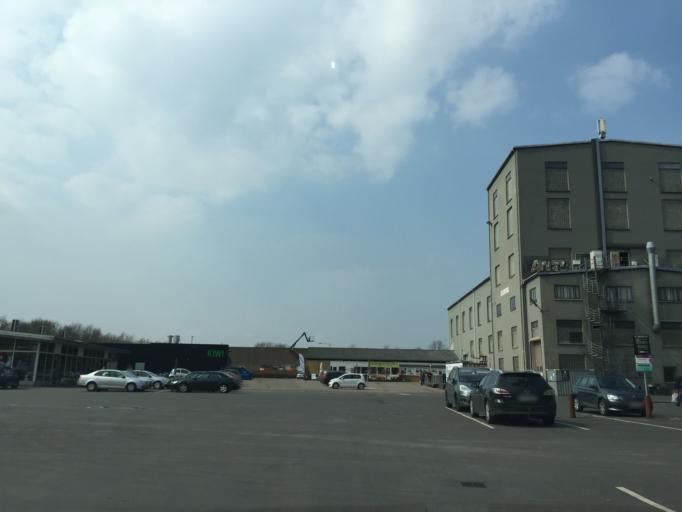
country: DK
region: South Denmark
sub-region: Odense Kommune
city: Odense
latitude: 55.3933
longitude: 10.3685
